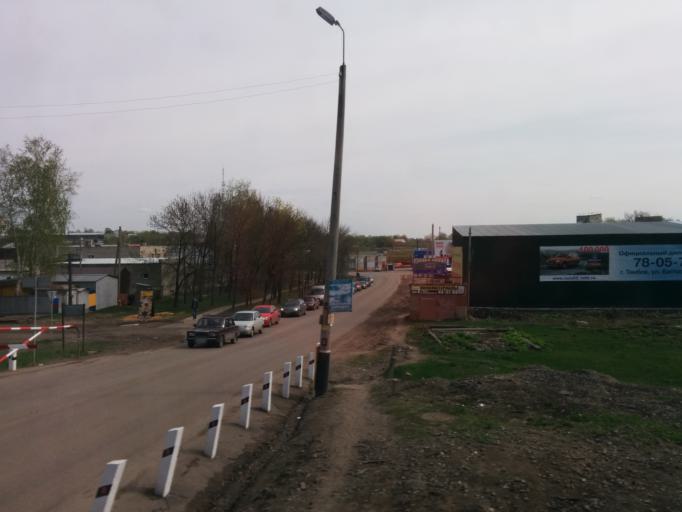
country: RU
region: Tambov
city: Tambov
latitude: 52.7356
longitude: 41.4100
